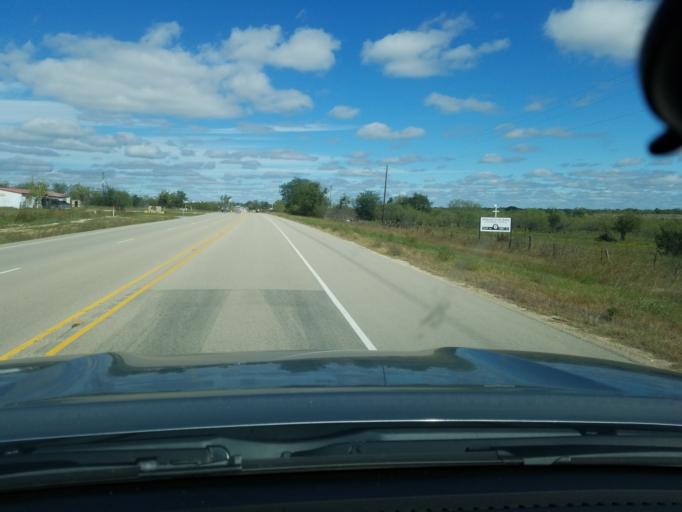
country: US
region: Texas
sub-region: Hamilton County
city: Hamilton
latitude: 31.6818
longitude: -98.1326
